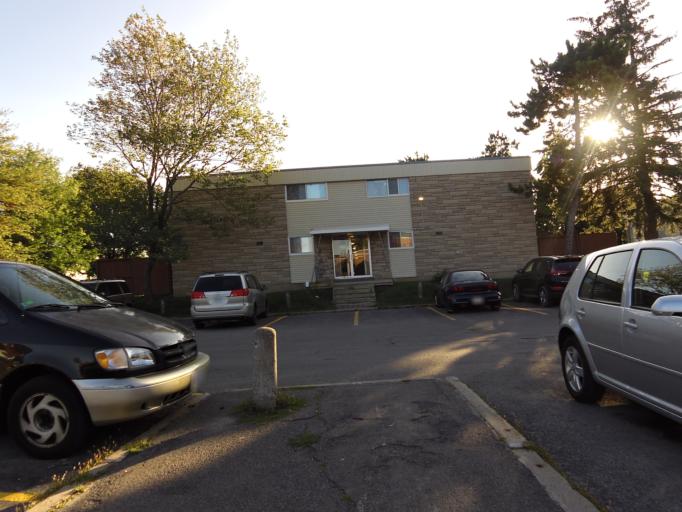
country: CA
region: Ontario
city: Ottawa
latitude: 45.3624
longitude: -75.7151
